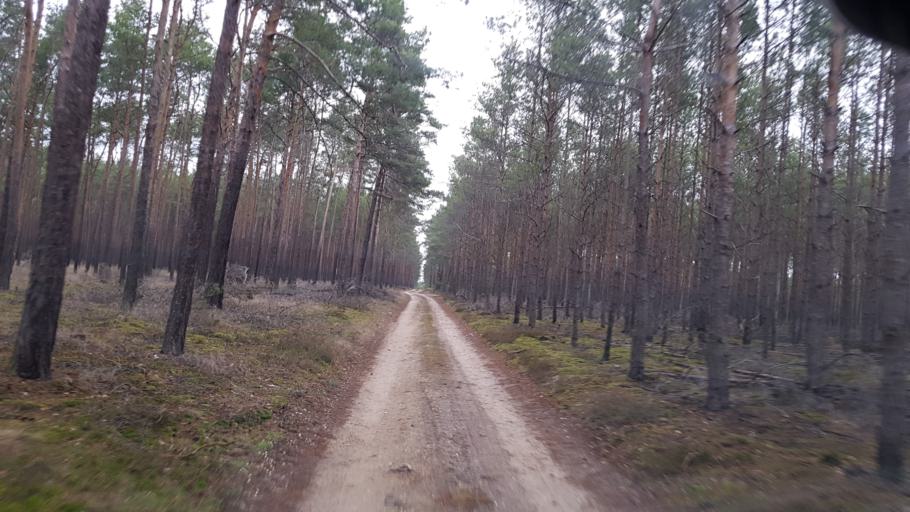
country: DE
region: Brandenburg
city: Finsterwalde
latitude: 51.6201
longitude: 13.6475
